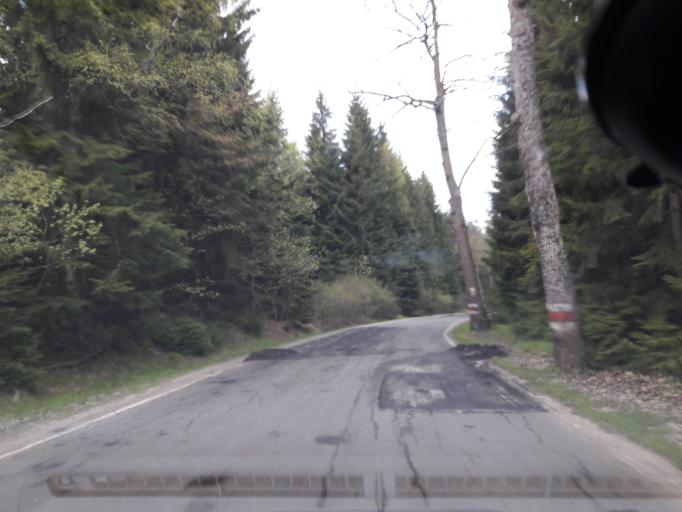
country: PL
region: Lower Silesian Voivodeship
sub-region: Powiat klodzki
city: Radkow
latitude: 50.4656
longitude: 16.3463
